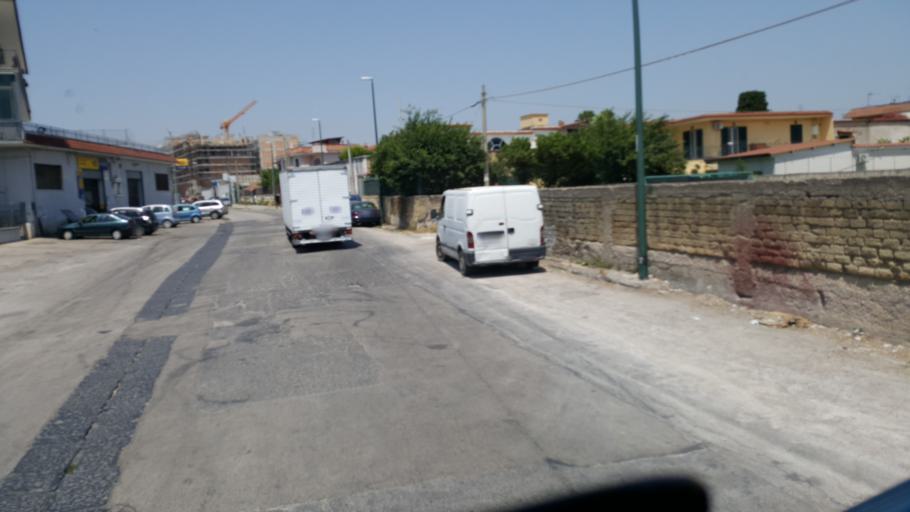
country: IT
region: Campania
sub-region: Provincia di Napoli
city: Arpino
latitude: 40.8727
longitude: 14.3083
